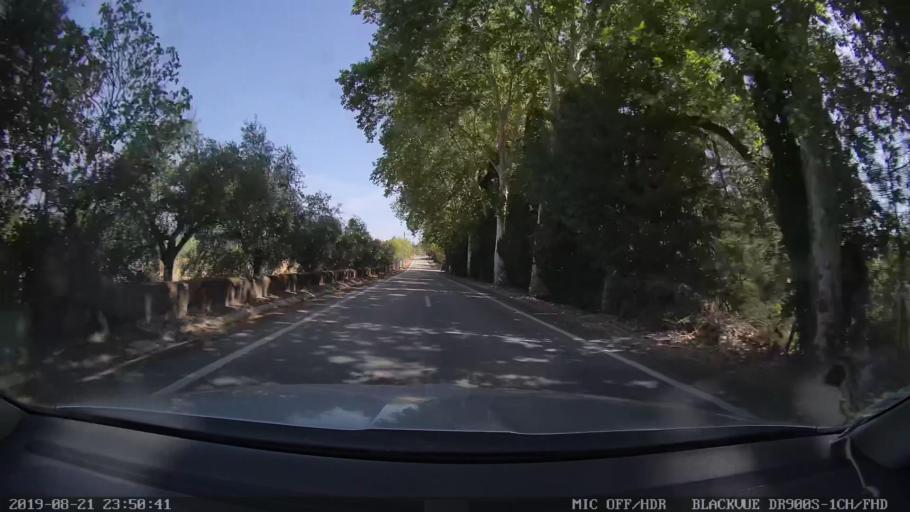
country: PT
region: Castelo Branco
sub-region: Idanha-A-Nova
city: Idanha-a-Nova
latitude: 39.8933
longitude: -7.2401
